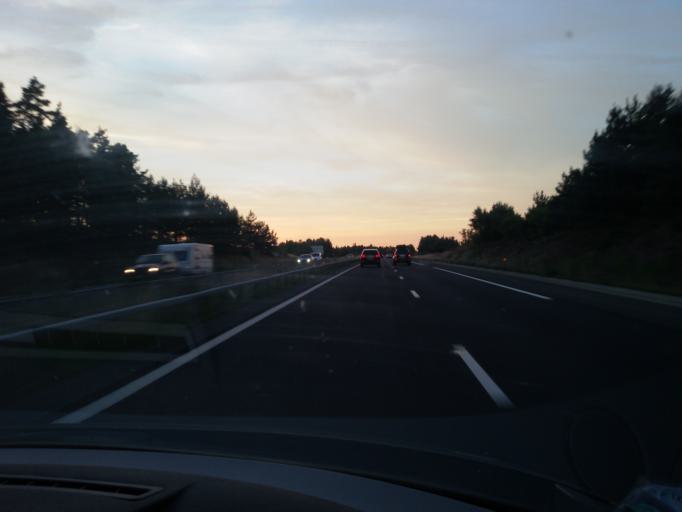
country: FR
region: Languedoc-Roussillon
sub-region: Departement de la Lozere
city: Le Malzieu-Ville
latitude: 44.8281
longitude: 3.2633
